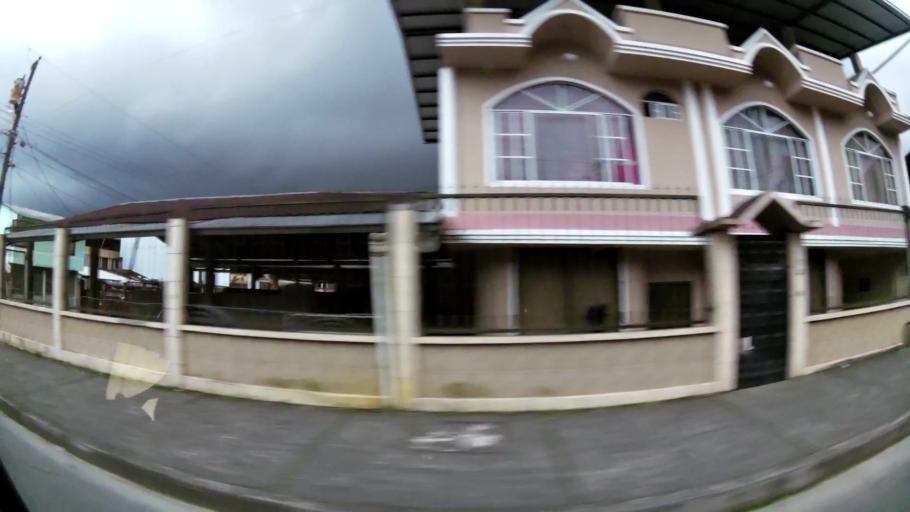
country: EC
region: Pastaza
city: Puyo
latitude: -1.4840
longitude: -78.0066
